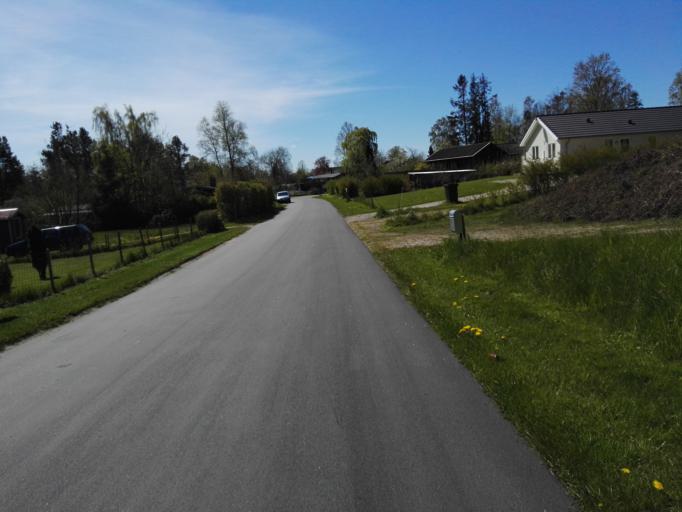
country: DK
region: Capital Region
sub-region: Frederikssund Kommune
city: Frederikssund
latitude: 55.9000
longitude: 12.0542
